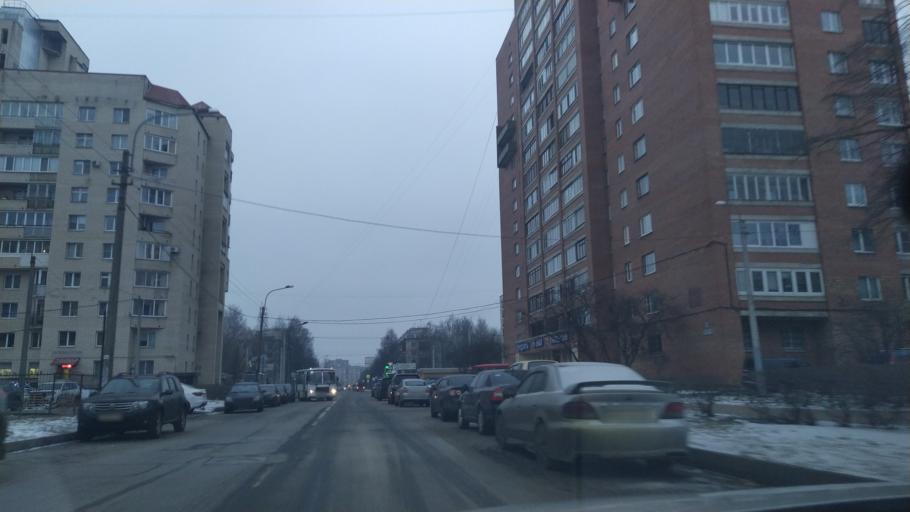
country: RU
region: St.-Petersburg
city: Grazhdanka
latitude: 60.0438
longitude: 30.4049
